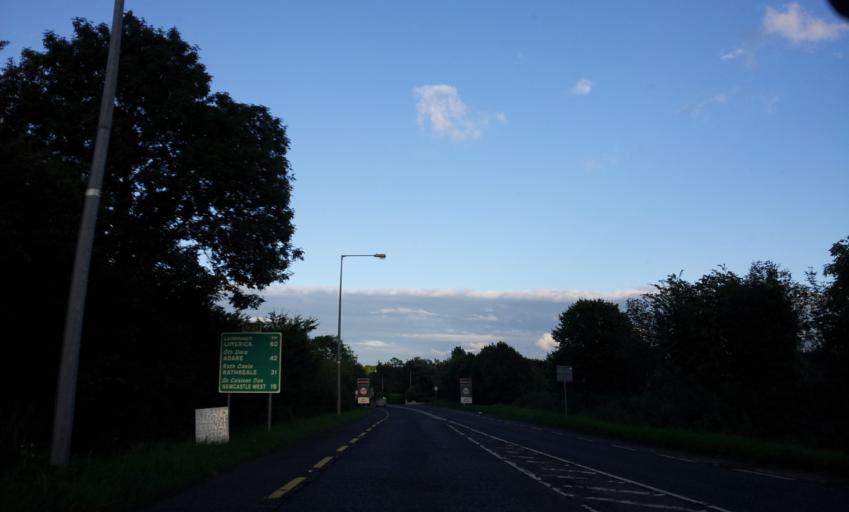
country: IE
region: Munster
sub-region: County Limerick
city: Abbeyfeale
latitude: 52.3888
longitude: -9.2812
